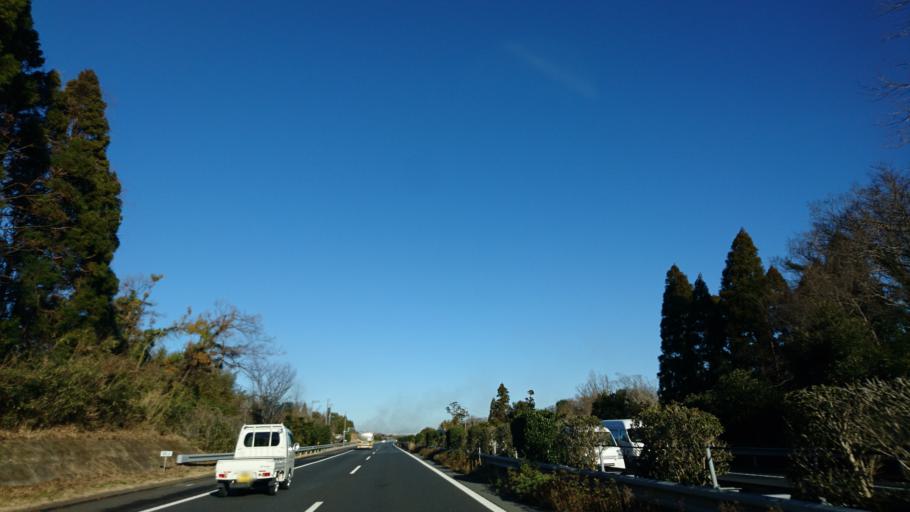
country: JP
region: Chiba
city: Ichihara
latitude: 35.4708
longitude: 140.0838
